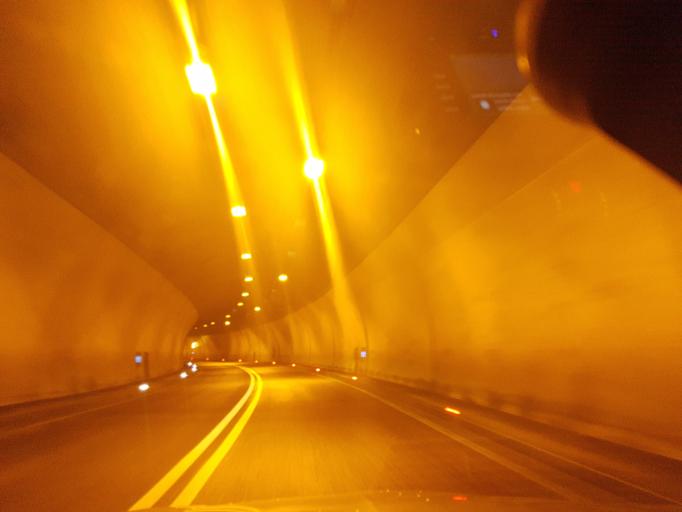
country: IT
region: Trentino-Alto Adige
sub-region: Bolzano
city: Santa Cristina Valgardena
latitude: 46.5558
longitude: 11.7272
